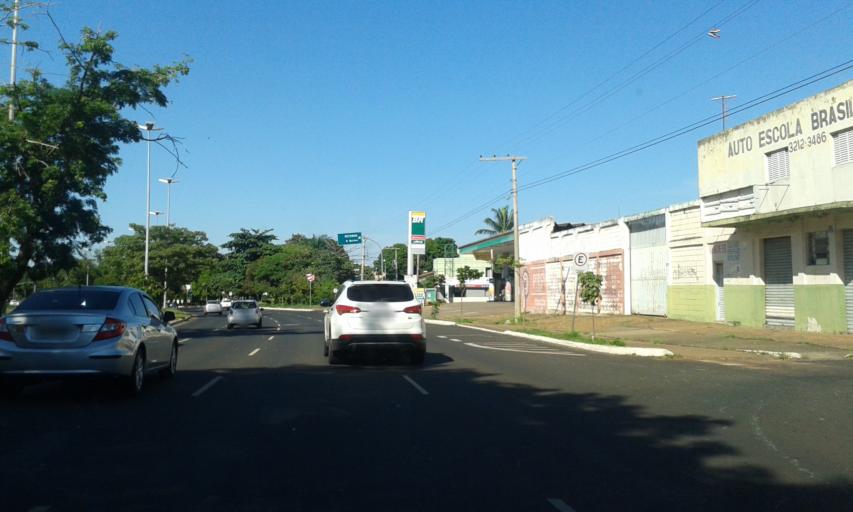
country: BR
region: Minas Gerais
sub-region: Uberlandia
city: Uberlandia
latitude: -18.9015
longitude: -48.2601
